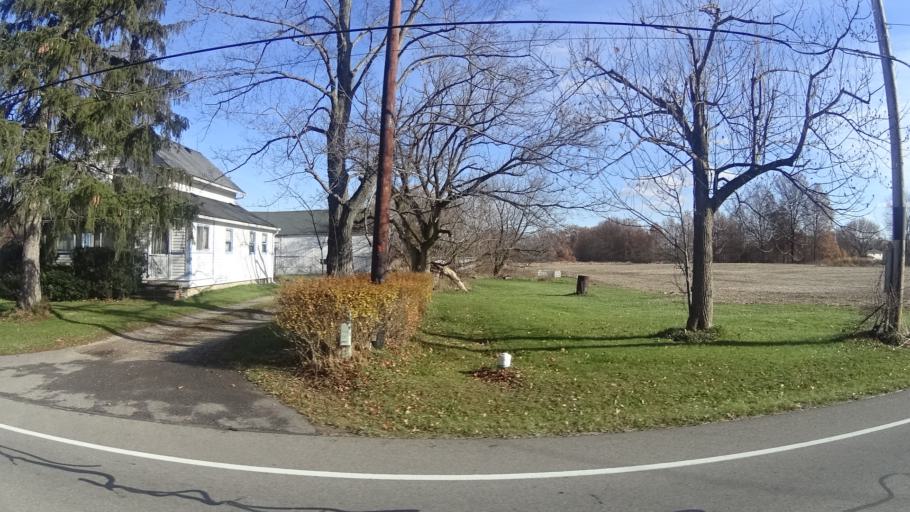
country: US
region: Ohio
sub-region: Lorain County
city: Eaton Estates
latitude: 41.2986
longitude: -81.9817
